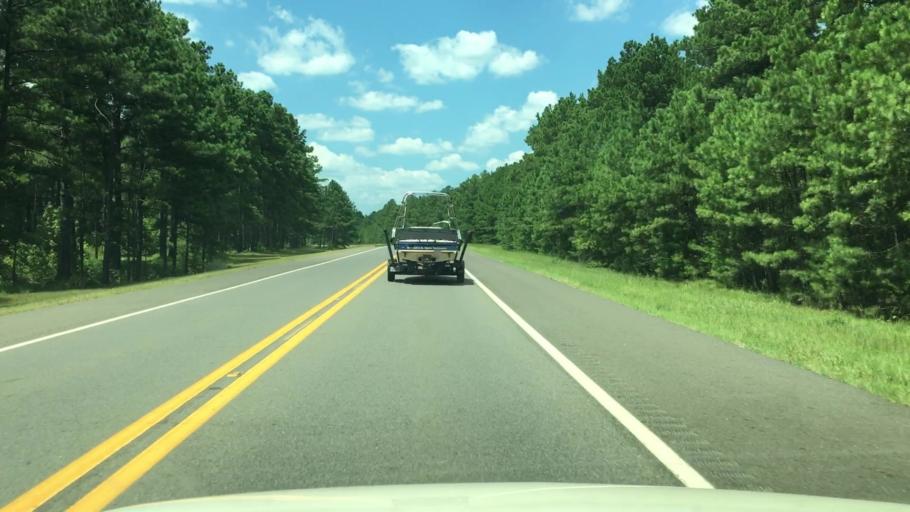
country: US
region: Arkansas
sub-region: Clark County
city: Arkadelphia
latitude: 34.2228
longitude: -93.0873
